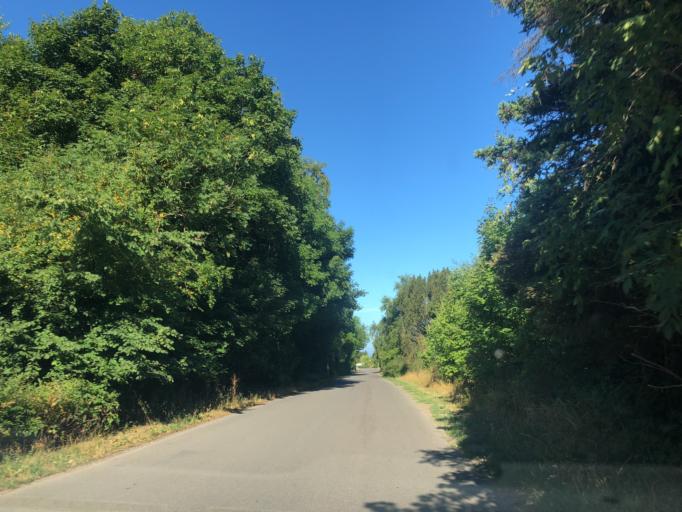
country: DK
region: Zealand
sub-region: Slagelse Kommune
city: Forlev
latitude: 55.3796
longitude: 11.2111
